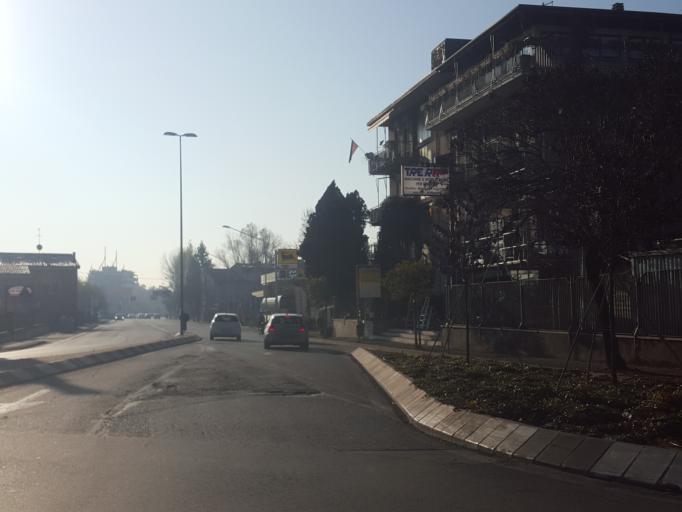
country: IT
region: Veneto
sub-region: Provincia di Vicenza
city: Vicenza
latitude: 45.5567
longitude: 11.5635
